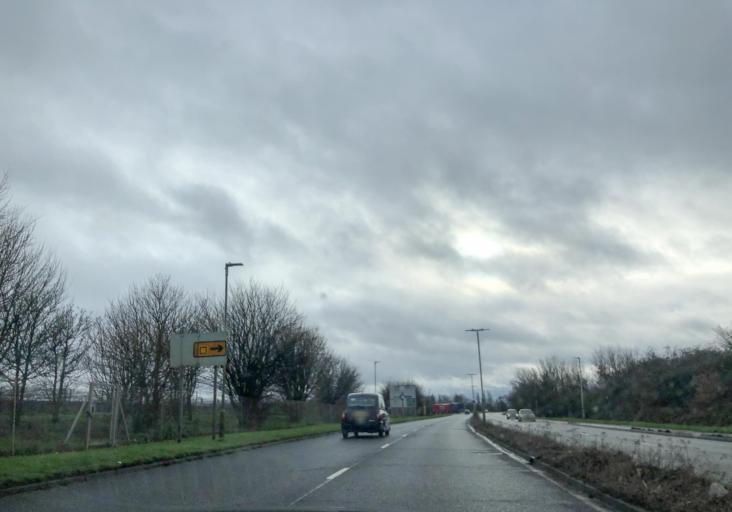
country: GB
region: England
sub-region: Surrey
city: Colnbrook
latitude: 51.4665
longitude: -0.4922
